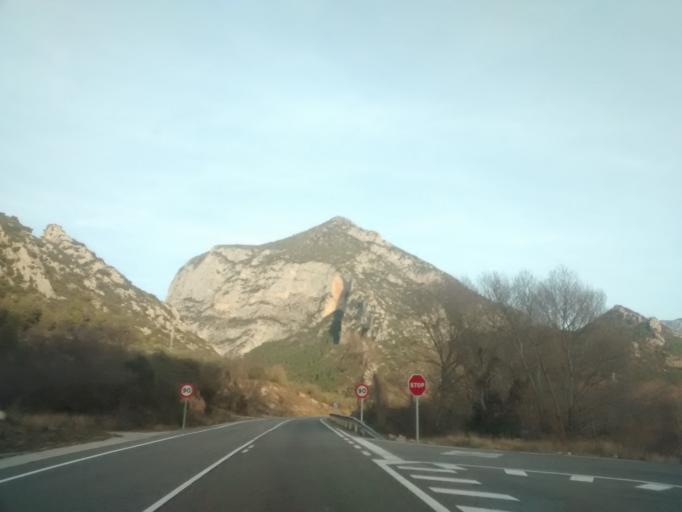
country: ES
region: Catalonia
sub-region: Provincia de Lleida
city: Coll de Nargo
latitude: 42.1796
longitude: 1.3188
